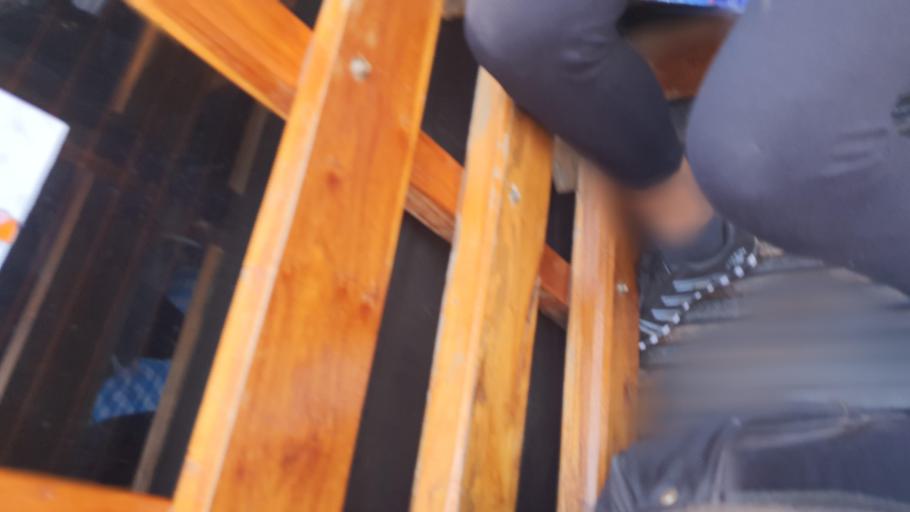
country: TH
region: Changwat Bueng Kan
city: Si Wilai
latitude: 18.2698
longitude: 103.8019
